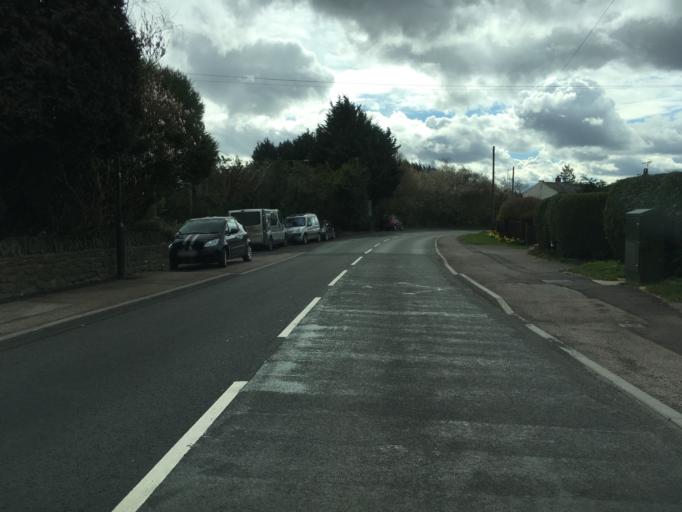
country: GB
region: England
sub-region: Gloucestershire
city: Coleford
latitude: 51.8030
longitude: -2.6003
